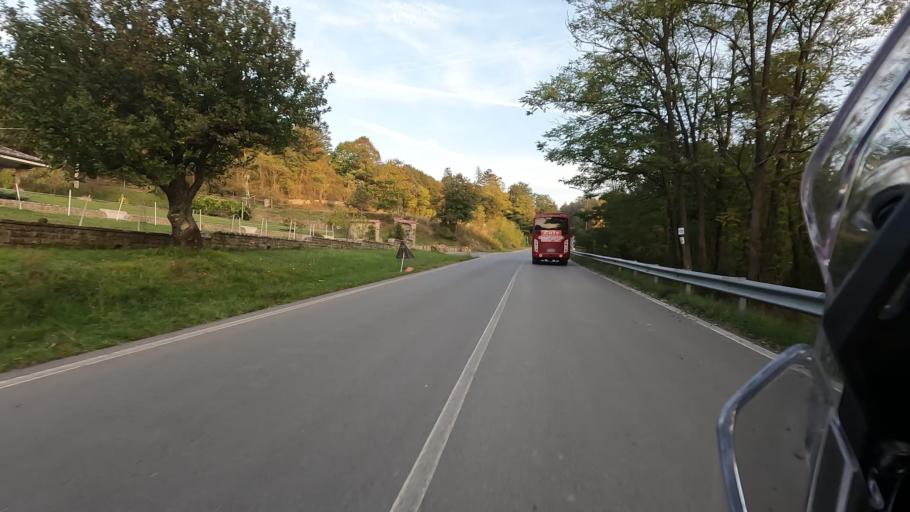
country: IT
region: Liguria
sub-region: Provincia di Savona
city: Pontinvrea
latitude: 44.4375
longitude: 8.4460
